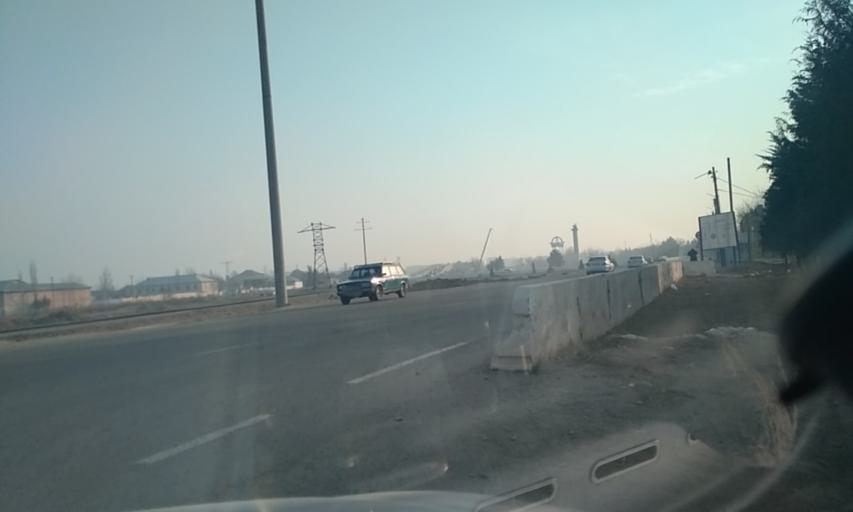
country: UZ
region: Sirdaryo
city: Guliston
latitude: 40.5068
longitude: 68.7536
